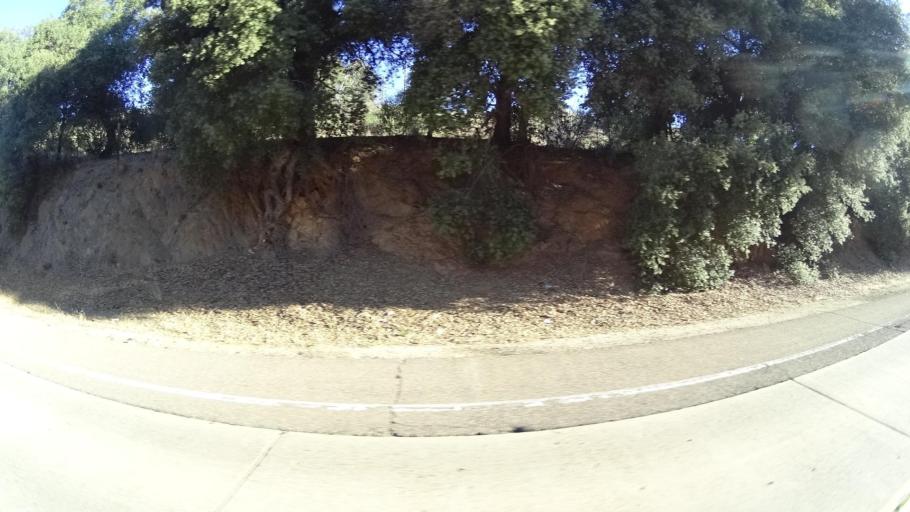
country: US
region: California
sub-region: San Diego County
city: Descanso
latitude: 32.8540
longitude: -116.5740
